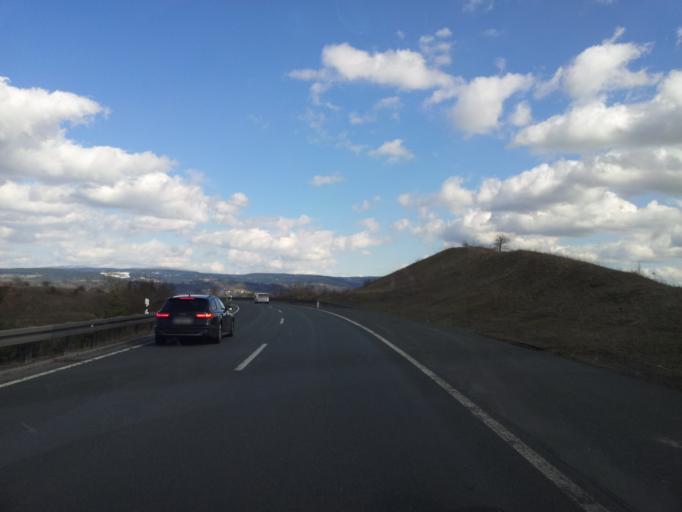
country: DE
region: Bavaria
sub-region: Upper Franconia
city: Harsdorf
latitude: 50.0247
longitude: 11.6015
